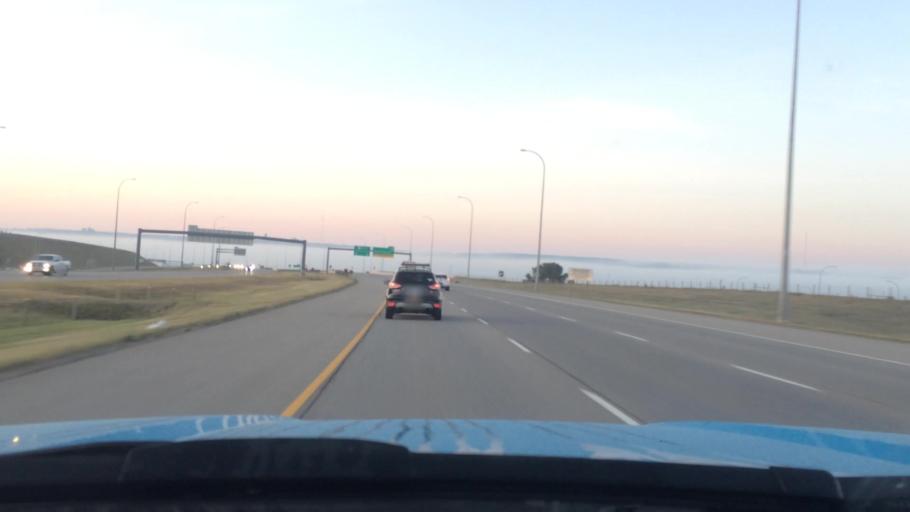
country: CA
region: Alberta
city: Calgary
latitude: 51.1217
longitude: -114.2317
